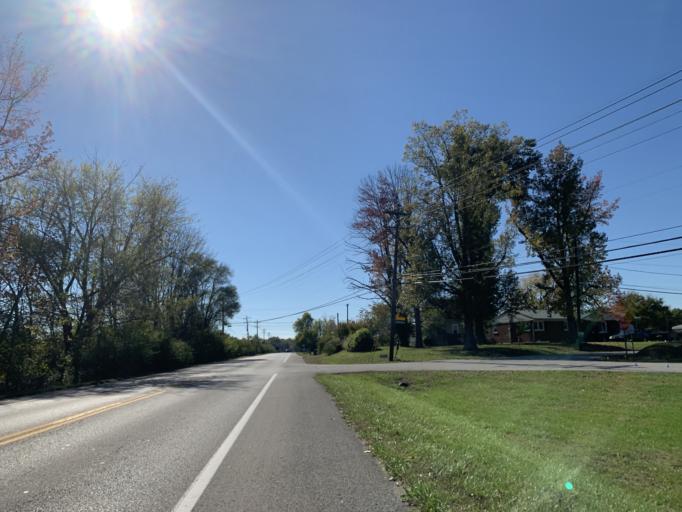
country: US
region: Kentucky
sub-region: Jefferson County
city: Saint Dennis
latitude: 38.2042
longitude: -85.8521
